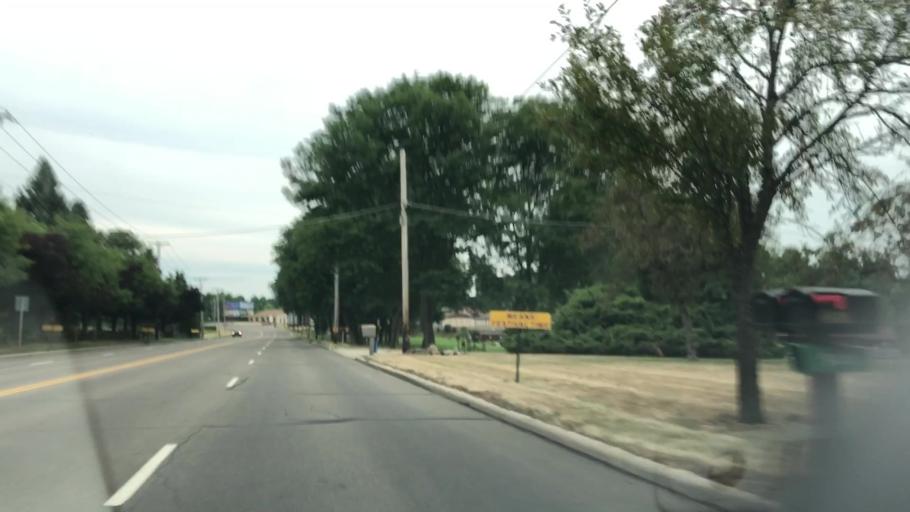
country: US
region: Ohio
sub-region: Stark County
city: Uniontown
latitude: 40.9644
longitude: -81.4088
